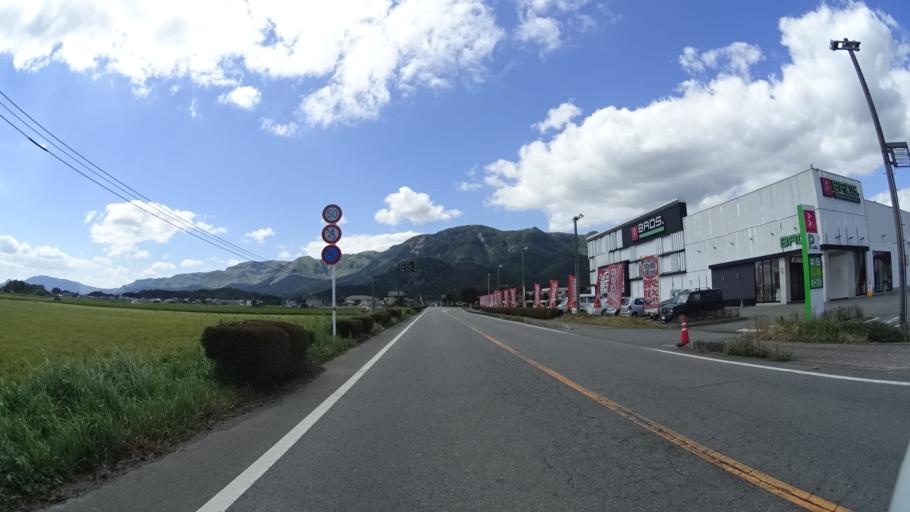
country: JP
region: Kumamoto
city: Aso
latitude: 32.9686
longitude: 131.0442
